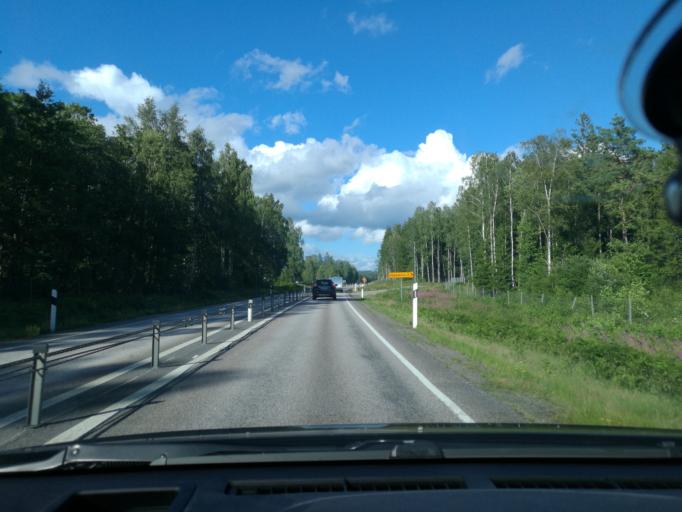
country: SE
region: Kronoberg
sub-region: Vaxjo Kommun
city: Rottne
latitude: 56.9851
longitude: 14.9880
